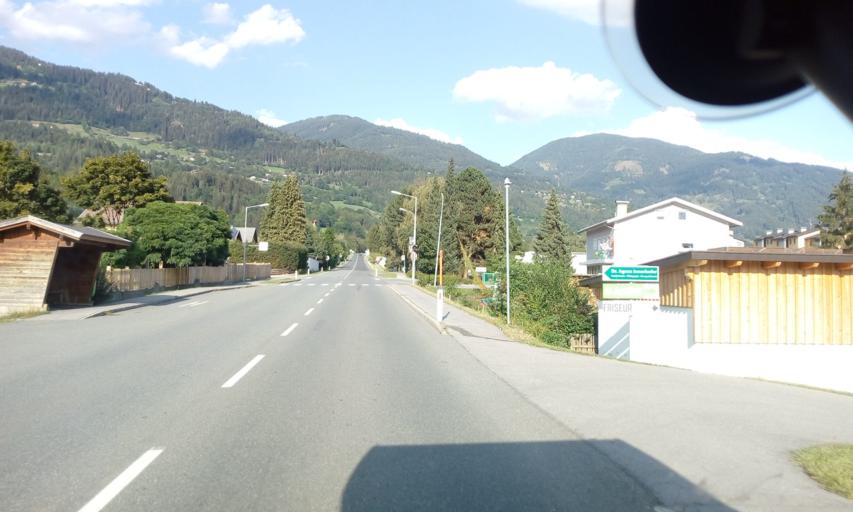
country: AT
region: Tyrol
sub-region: Politischer Bezirk Lienz
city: Tristach
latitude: 46.8314
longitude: 12.8139
